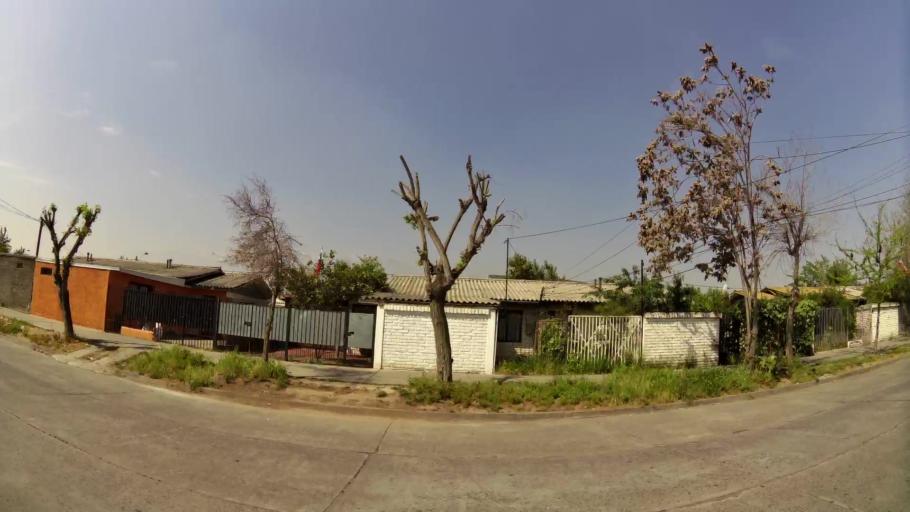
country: CL
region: Santiago Metropolitan
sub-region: Provincia de Santiago
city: La Pintana
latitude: -33.5447
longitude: -70.5984
